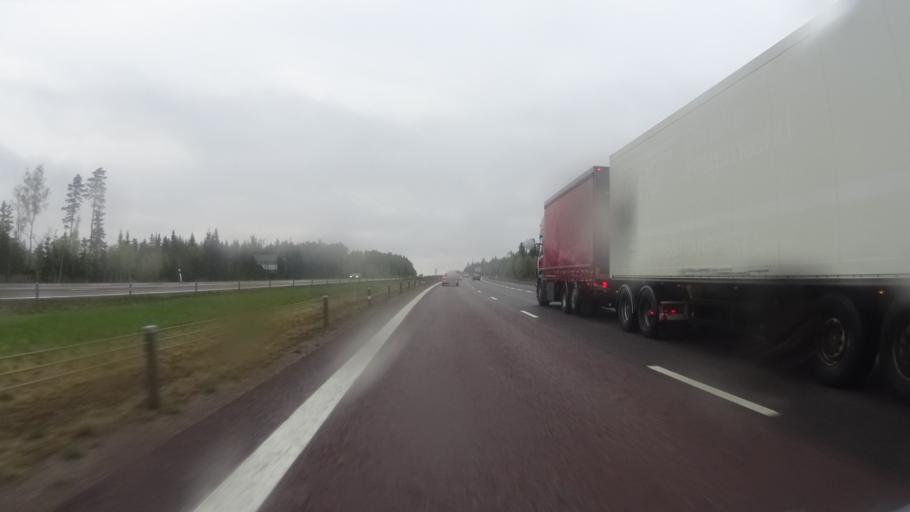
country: SE
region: Kronoberg
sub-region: Ljungby Kommun
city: Ljungby
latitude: 56.7018
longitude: 13.8358
